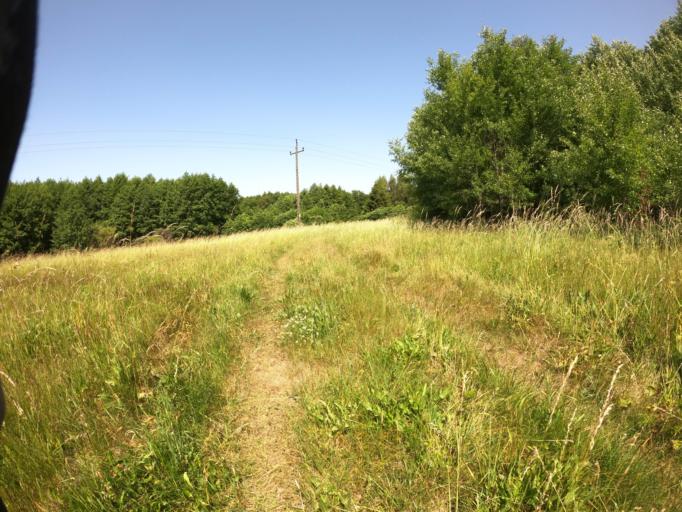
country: PL
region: West Pomeranian Voivodeship
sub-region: Powiat mysliborski
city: Mysliborz
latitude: 52.8932
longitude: 14.8075
